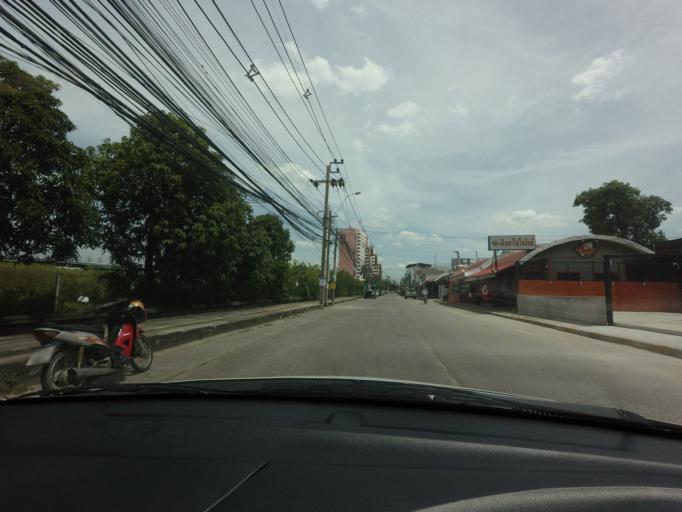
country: TH
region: Bangkok
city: Lak Si
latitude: 13.8976
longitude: 100.5465
